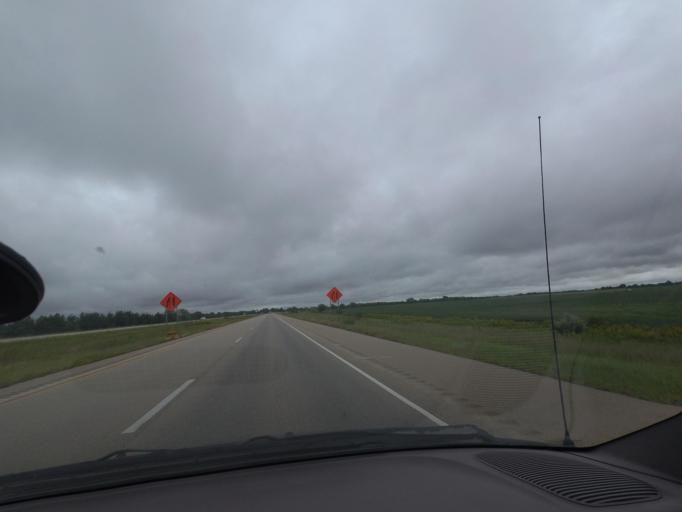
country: US
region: Illinois
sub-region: Piatt County
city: Cerro Gordo
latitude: 39.9678
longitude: -88.8122
